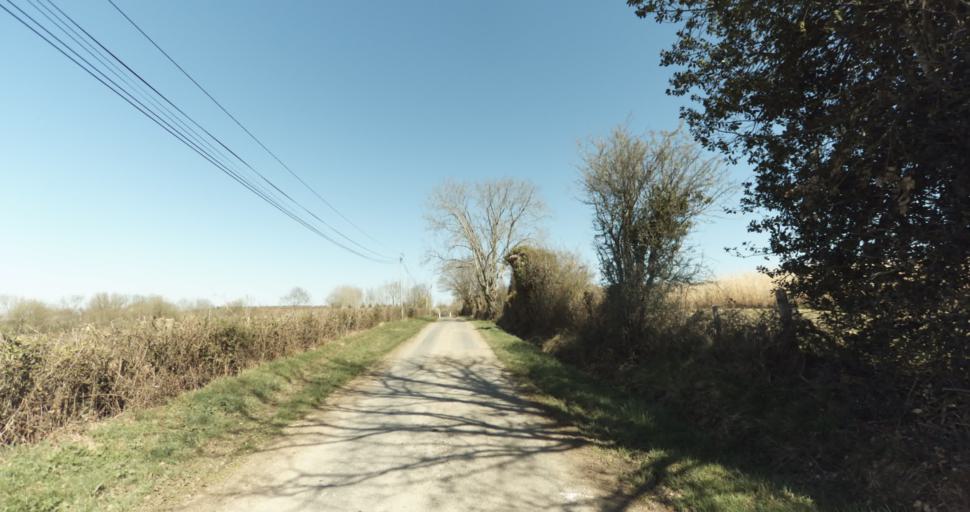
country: FR
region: Lower Normandy
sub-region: Departement du Calvados
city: Livarot
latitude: 49.0150
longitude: 0.1045
